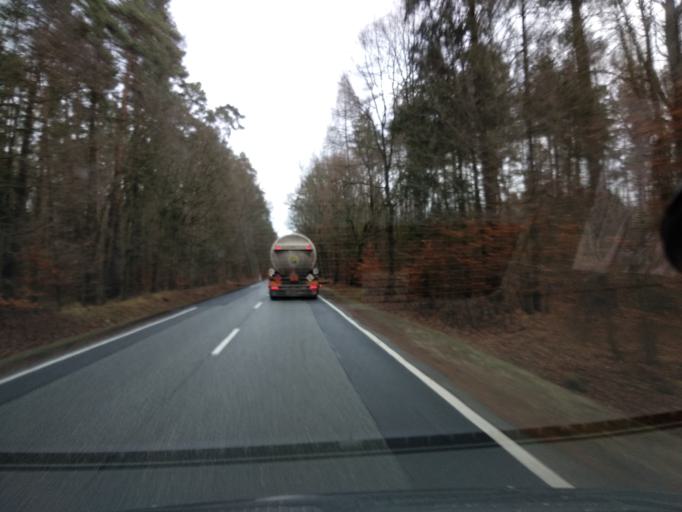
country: PL
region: Lower Silesian Voivodeship
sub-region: Powiat olesnicki
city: Twardogora
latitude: 51.3202
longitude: 17.5642
